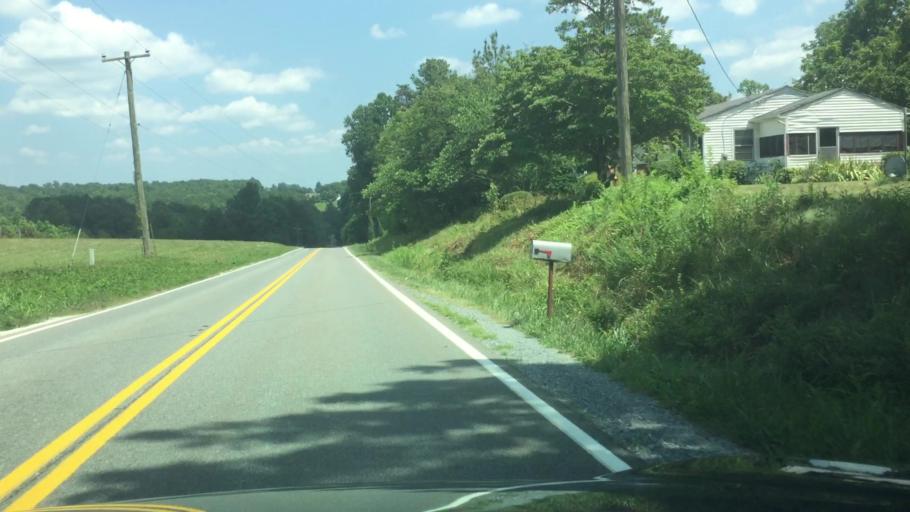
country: US
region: Virginia
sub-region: Appomattox County
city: Appomattox
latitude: 37.3419
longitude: -78.8963
